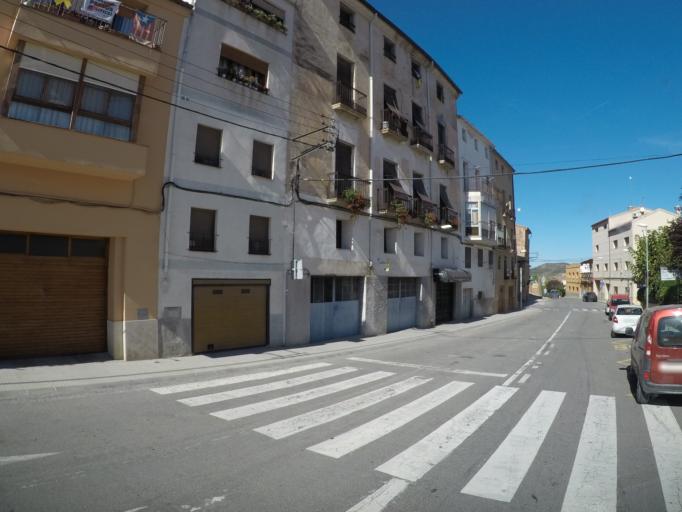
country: ES
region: Catalonia
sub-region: Provincia de Tarragona
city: Falset
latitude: 41.1463
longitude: 0.8211
